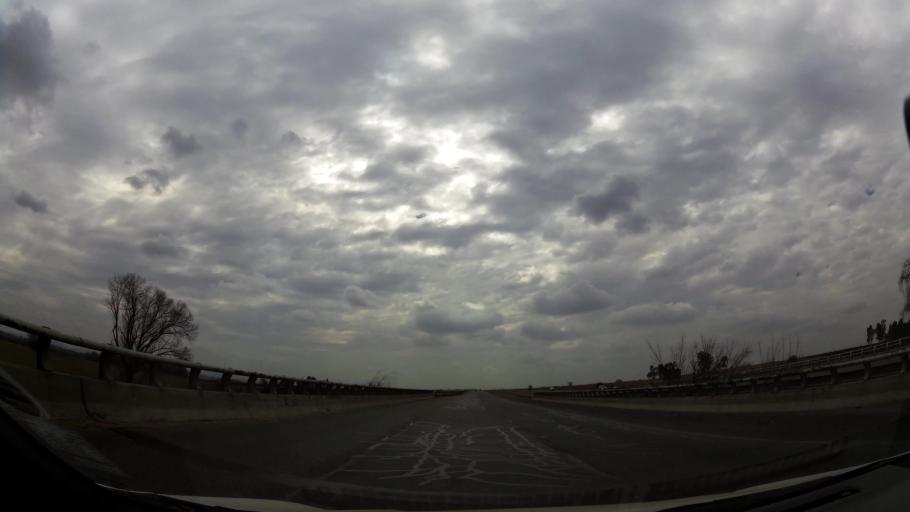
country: ZA
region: Gauteng
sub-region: Sedibeng District Municipality
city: Meyerton
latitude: -26.4016
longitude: 28.0801
